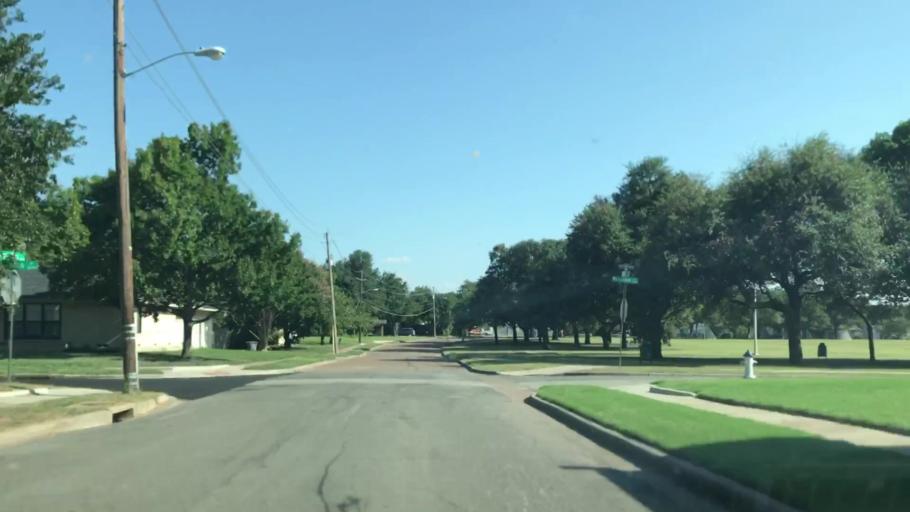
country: US
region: Texas
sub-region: Dallas County
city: Garland
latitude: 32.8285
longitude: -96.6719
